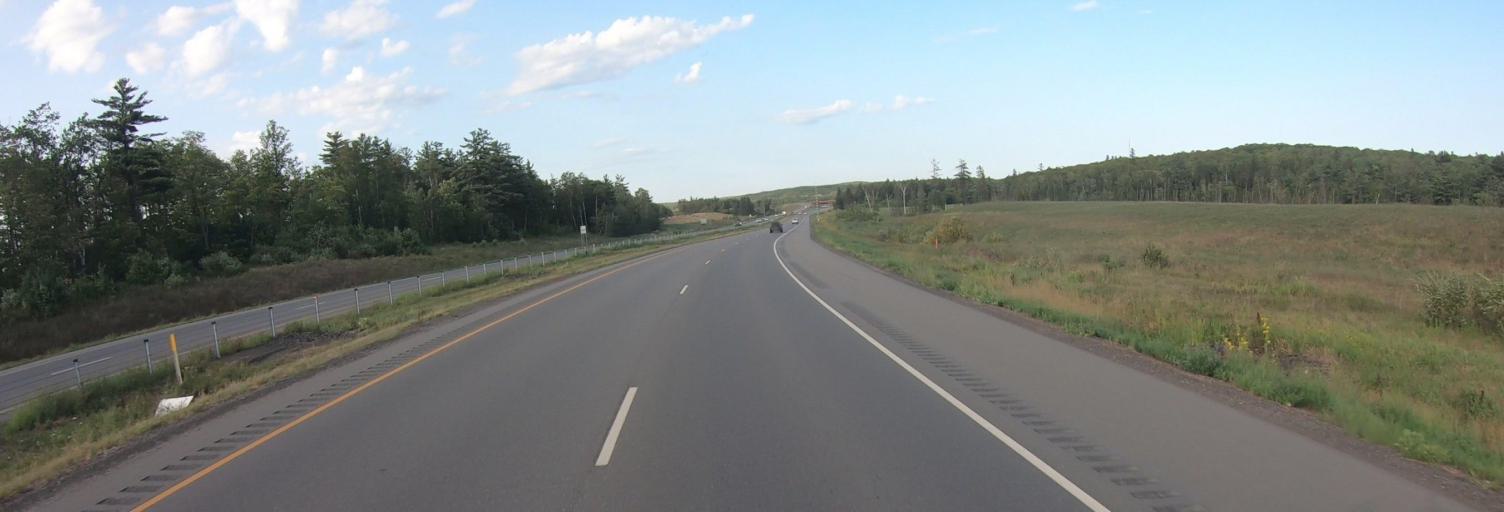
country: US
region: Minnesota
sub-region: Saint Louis County
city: Virginia
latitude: 47.4954
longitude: -92.5285
